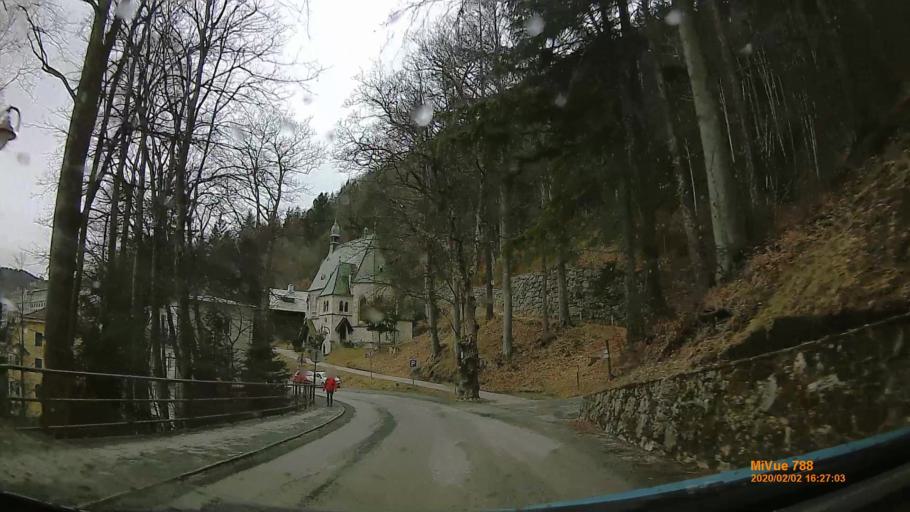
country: AT
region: Lower Austria
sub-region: Politischer Bezirk Neunkirchen
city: Semmering
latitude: 47.6396
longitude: 15.8264
